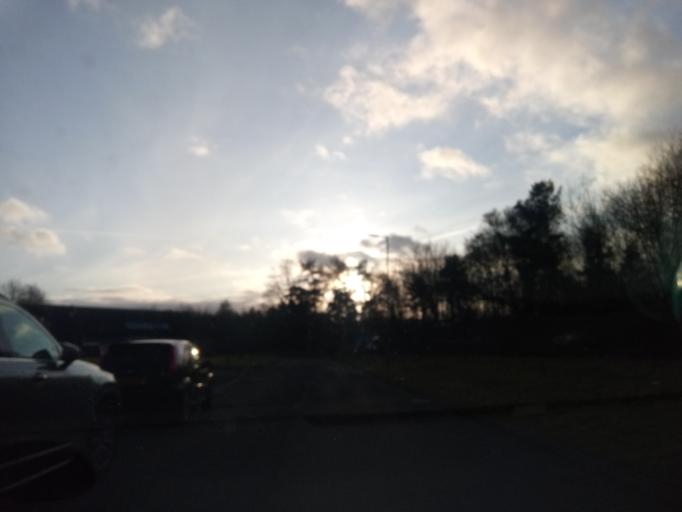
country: GB
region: Scotland
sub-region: The Scottish Borders
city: Melrose
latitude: 55.6046
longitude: -2.7578
